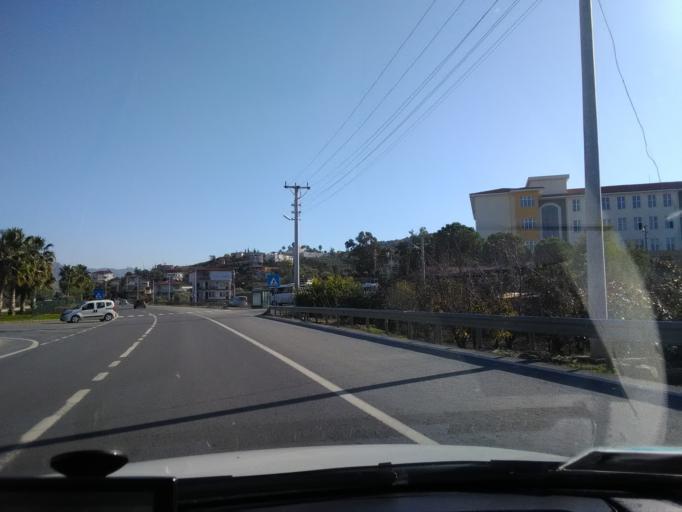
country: TR
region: Antalya
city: Gazipasa
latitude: 36.2576
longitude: 32.3256
